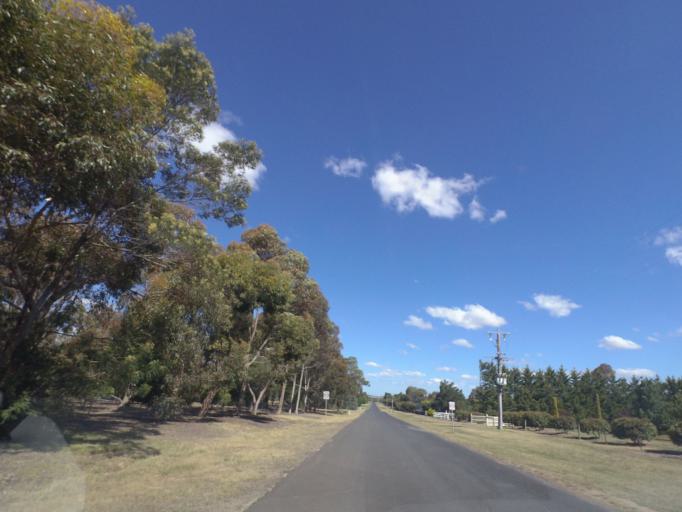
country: AU
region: Victoria
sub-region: Hume
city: Sunbury
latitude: -37.4565
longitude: 144.6638
